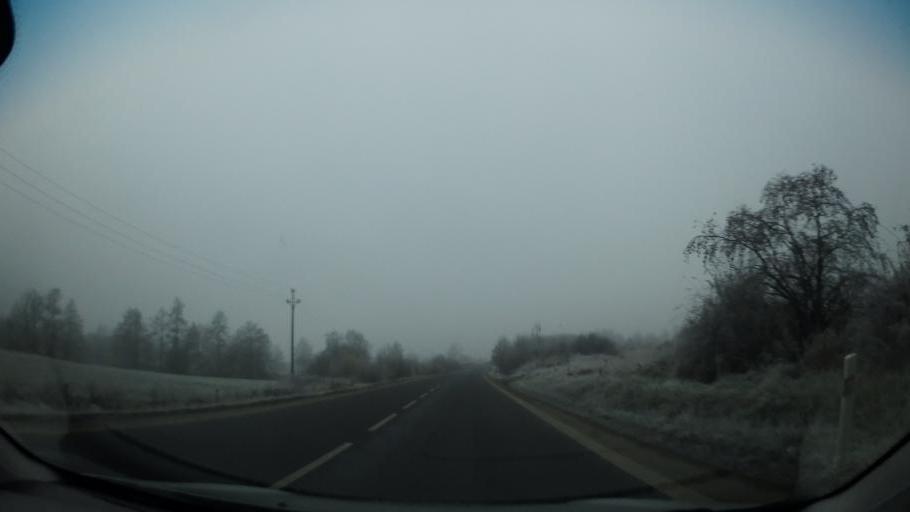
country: CZ
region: Vysocina
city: Budisov
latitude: 49.2655
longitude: 15.9340
